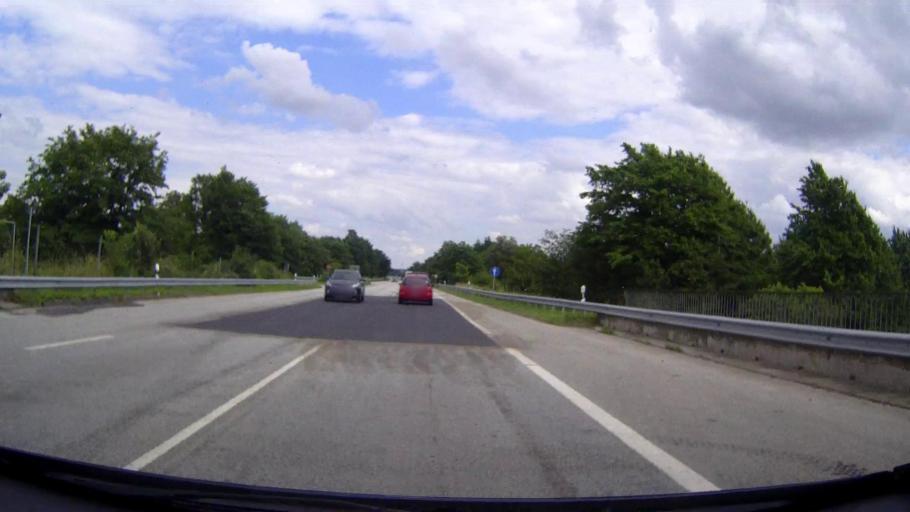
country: DE
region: Schleswig-Holstein
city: Klein Gladebrugge
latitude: 53.9226
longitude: 10.3340
